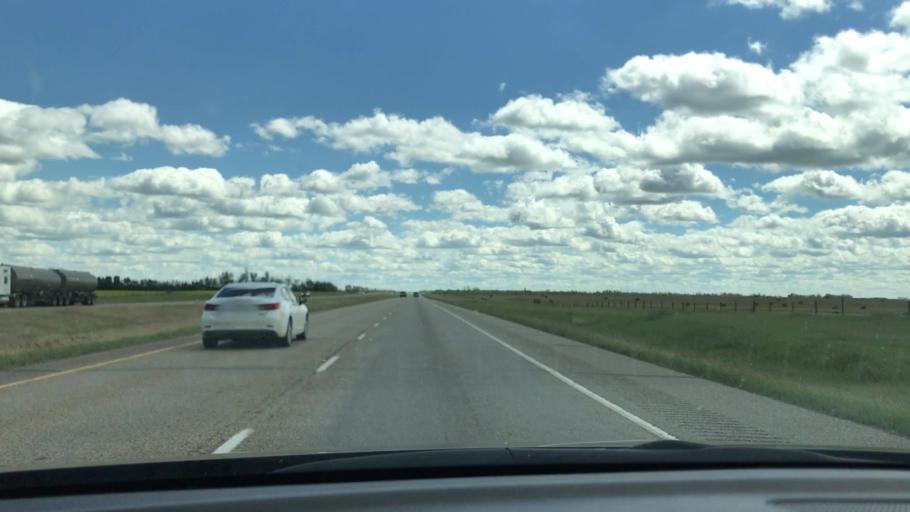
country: CA
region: Alberta
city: Leduc
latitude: 53.1620
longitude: -113.5985
